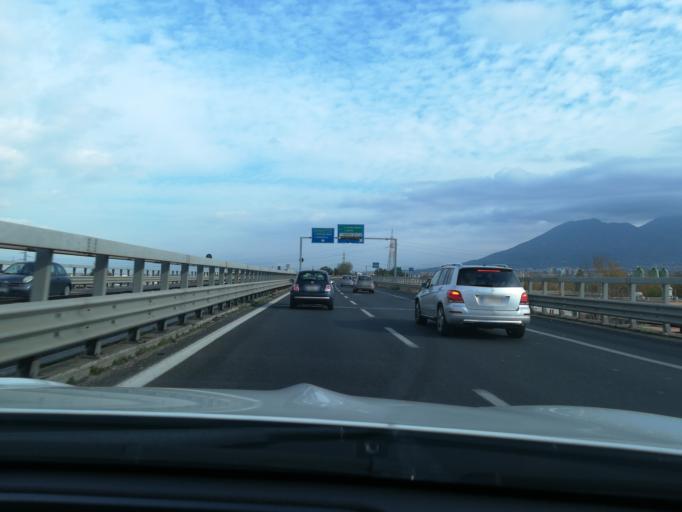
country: IT
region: Campania
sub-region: Provincia di Napoli
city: Arpino
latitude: 40.8666
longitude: 14.3151
